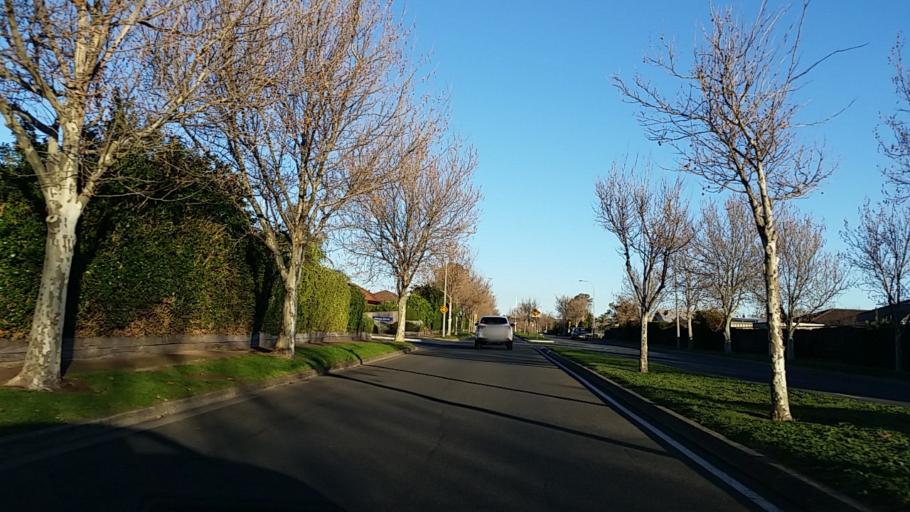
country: AU
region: South Australia
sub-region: Onkaparinga
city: Moana
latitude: -35.1949
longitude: 138.4835
